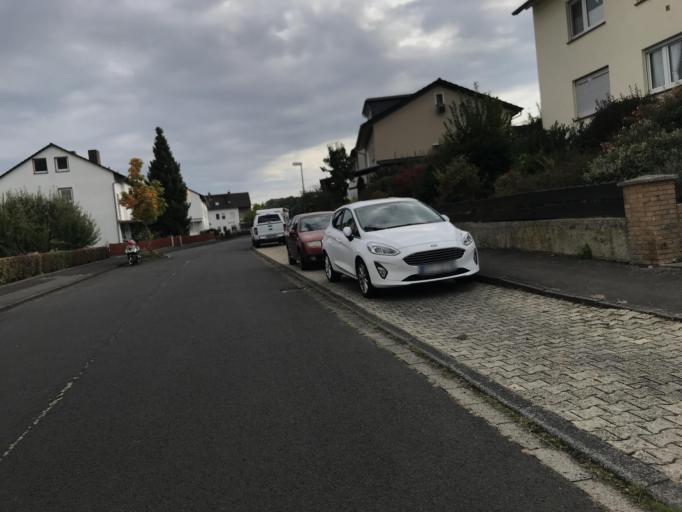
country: DE
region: Hesse
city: Borken
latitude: 51.0410
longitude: 9.2919
